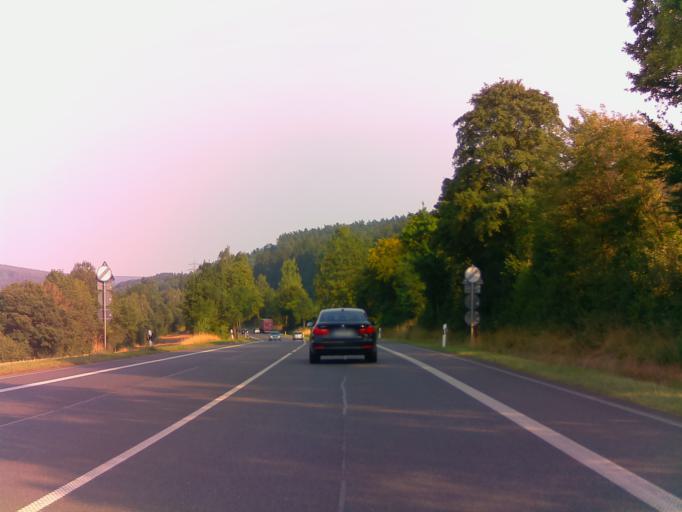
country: DE
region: Hesse
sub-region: Regierungsbezirk Kassel
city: Schenklengsfeld
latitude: 50.8634
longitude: 9.7879
